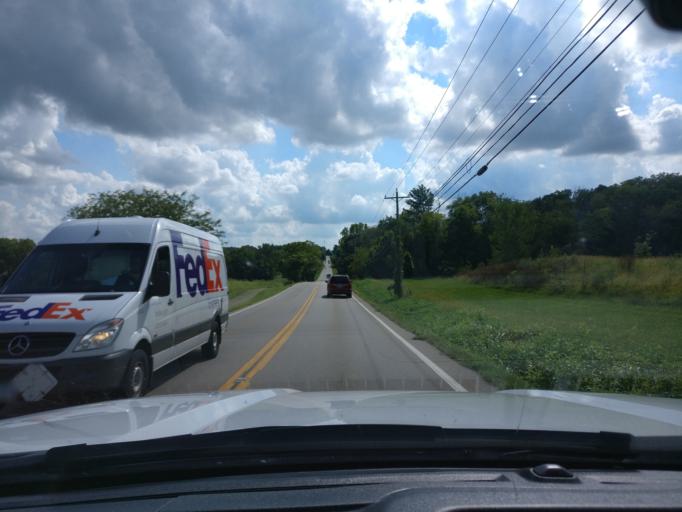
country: US
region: Ohio
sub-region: Warren County
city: Five Points
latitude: 39.5152
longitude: -84.1878
